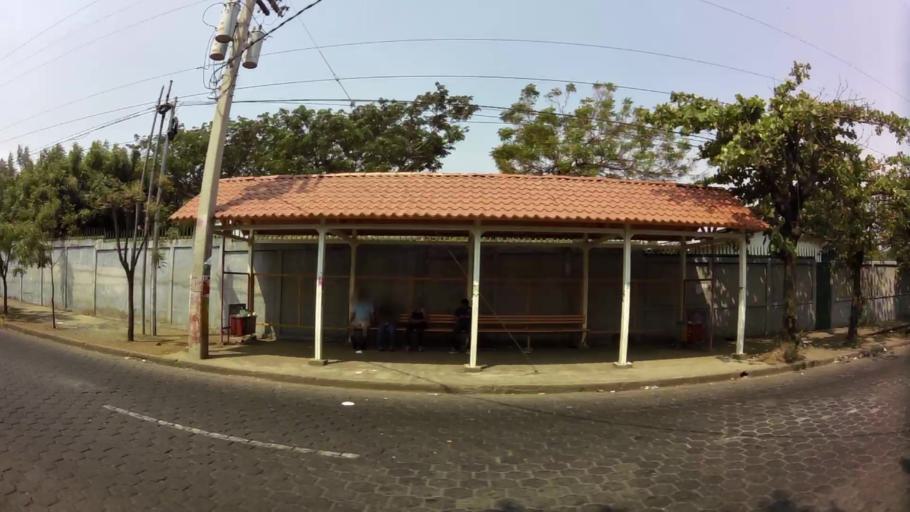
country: NI
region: Managua
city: Managua
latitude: 12.1427
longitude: -86.2963
